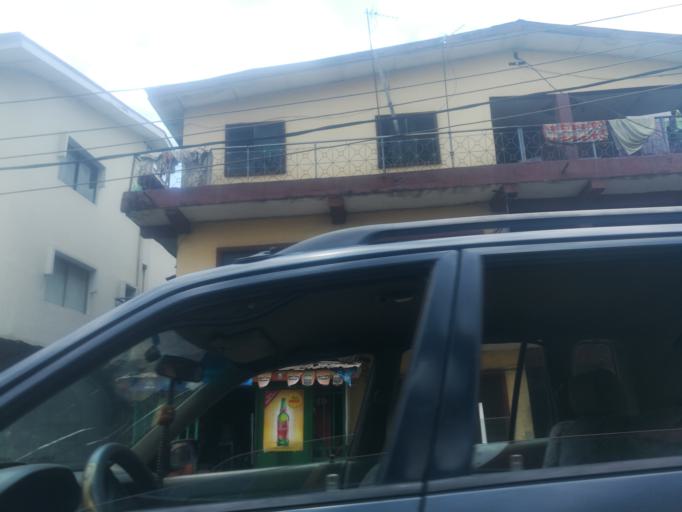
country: NG
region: Lagos
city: Somolu
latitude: 6.5531
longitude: 3.3920
